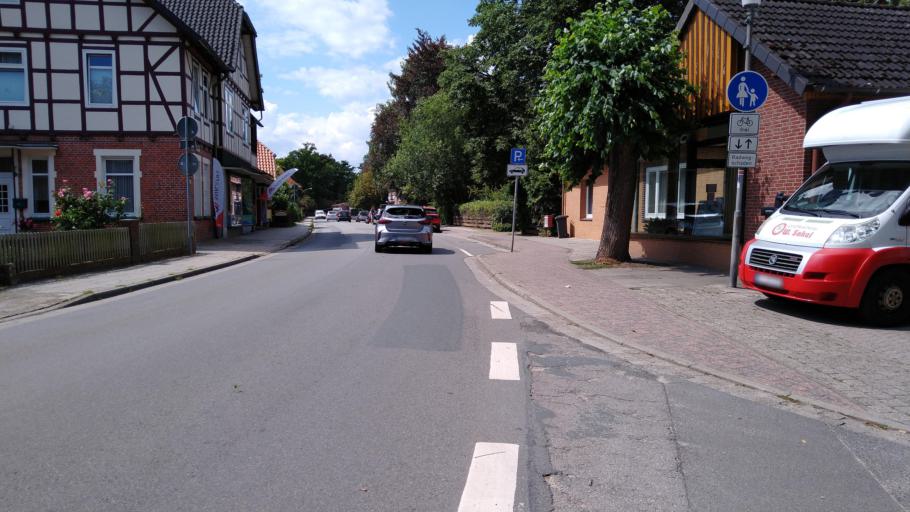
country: DE
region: Lower Saxony
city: Wienhausen
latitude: 52.5799
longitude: 10.1915
